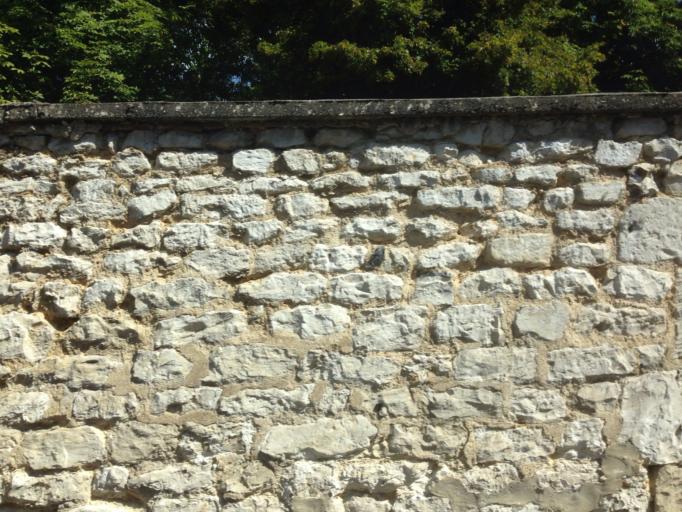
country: FR
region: Haute-Normandie
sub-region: Departement de l'Eure
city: Vernon
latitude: 49.0865
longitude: 1.4704
